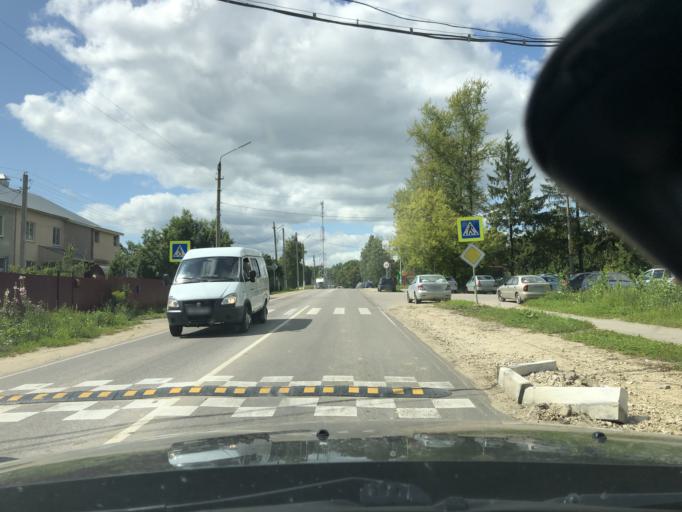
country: RU
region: Tula
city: Barsuki
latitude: 54.3385
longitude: 37.5513
